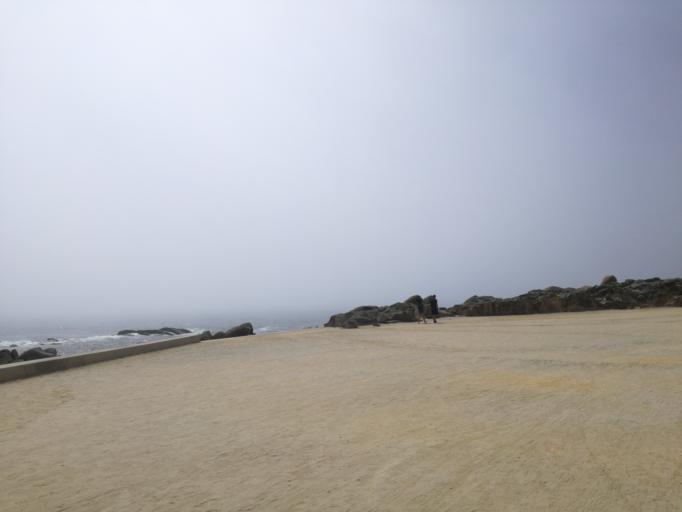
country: PT
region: Porto
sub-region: Vila do Conde
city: Vila do Conde
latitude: 41.3413
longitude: -8.7516
